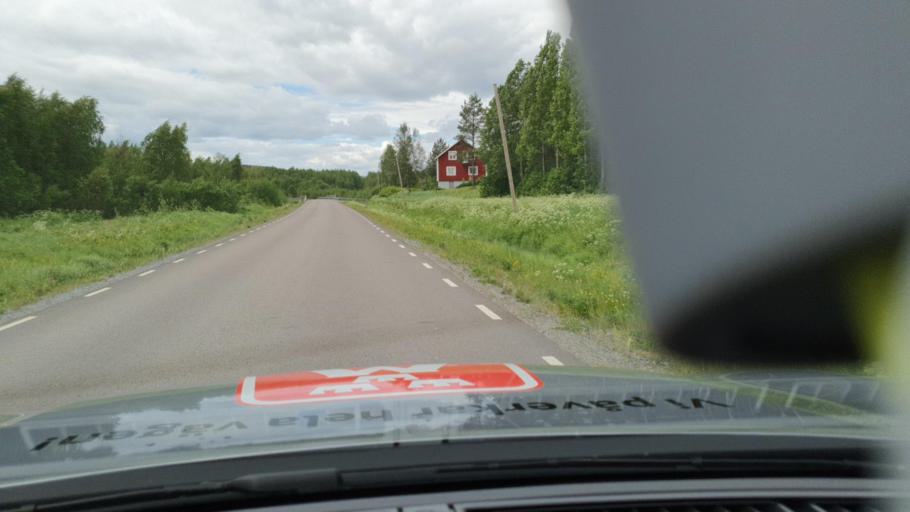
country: SE
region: Norrbotten
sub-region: Lulea Kommun
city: Sodra Sunderbyn
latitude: 65.8427
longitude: 21.9329
